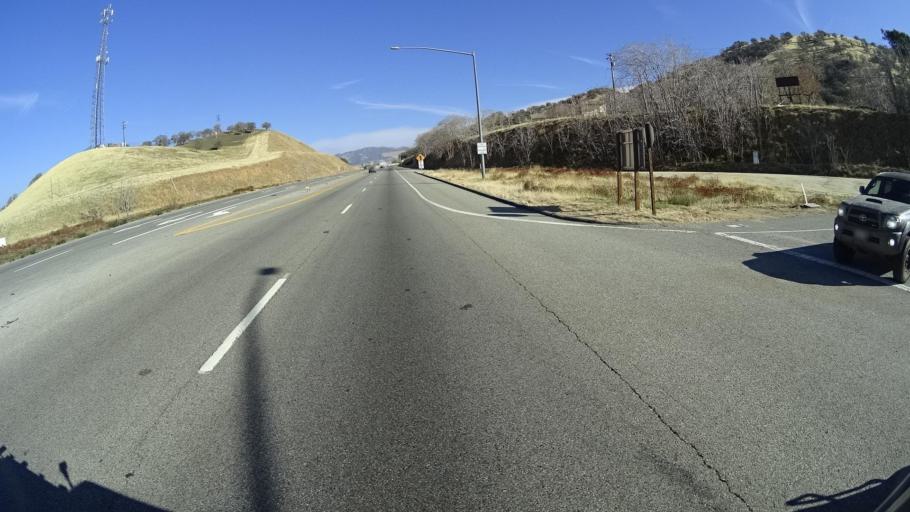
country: US
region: California
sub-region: Kern County
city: Bear Valley Springs
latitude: 35.2642
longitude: -118.6338
